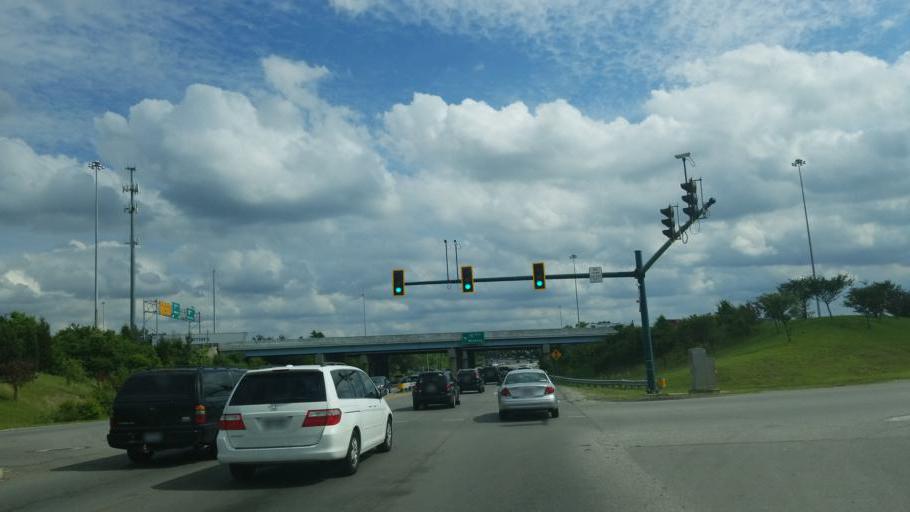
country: US
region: Ohio
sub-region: Franklin County
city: Reynoldsburg
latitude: 39.9347
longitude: -82.7896
